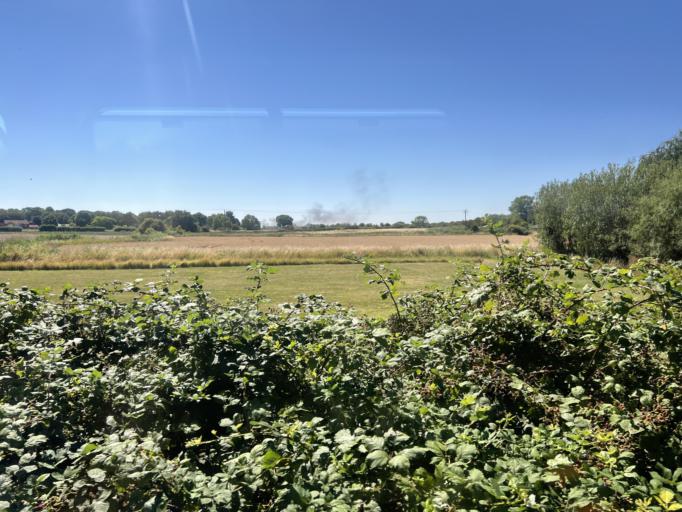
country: GB
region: England
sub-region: Lincolnshire
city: Wainfleet All Saints
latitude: 53.1085
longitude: 0.2273
